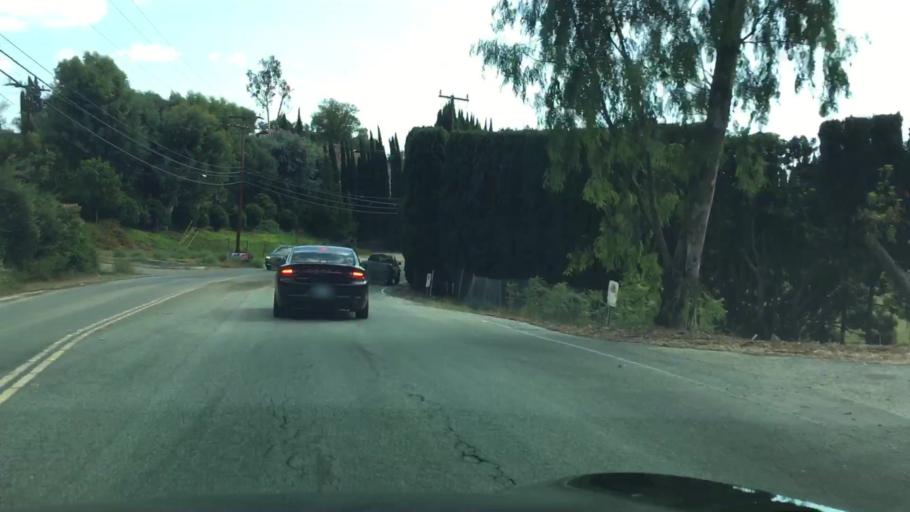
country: US
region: California
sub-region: Los Angeles County
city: La Habra Heights
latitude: 33.9623
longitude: -117.9588
